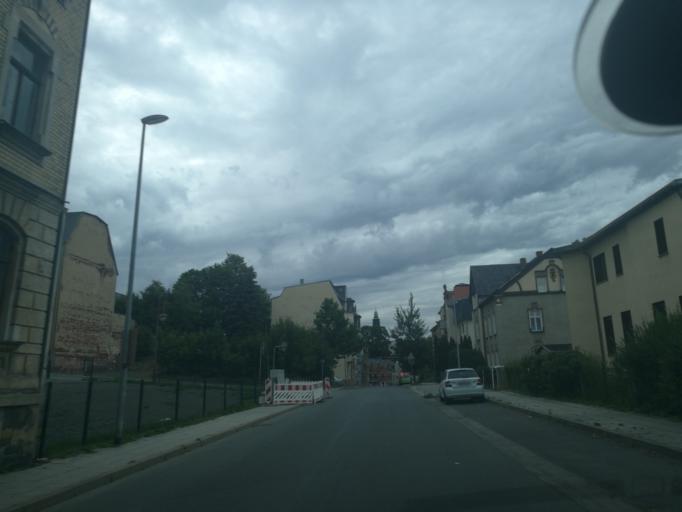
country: DE
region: Saxony
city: Adorf
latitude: 50.3169
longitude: 12.2545
